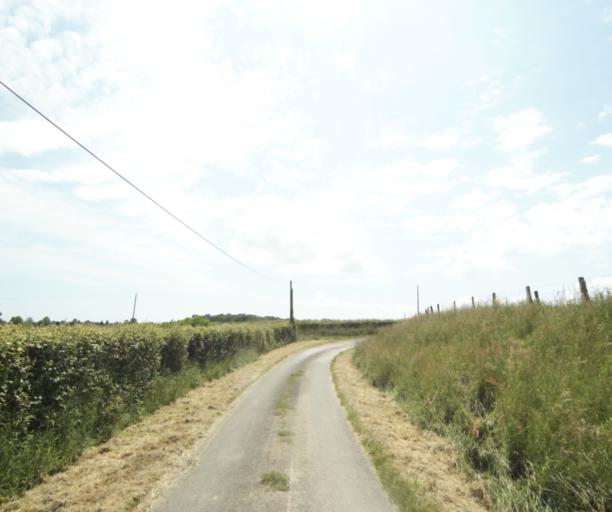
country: FR
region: Bourgogne
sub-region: Departement de Saone-et-Loire
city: Gueugnon
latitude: 46.5831
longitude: 4.1393
